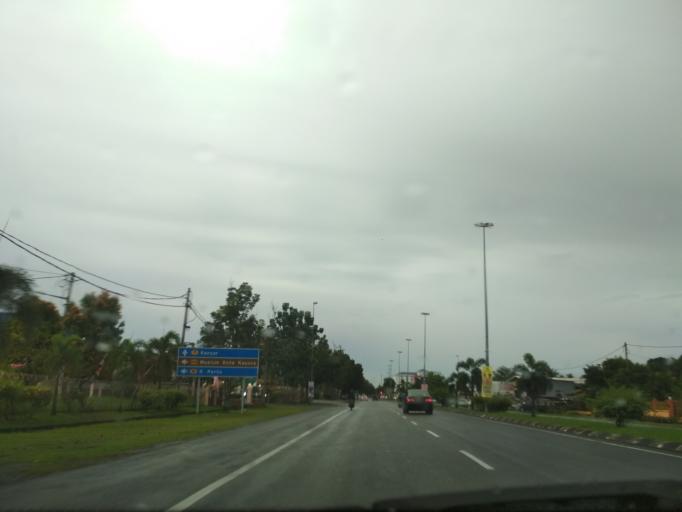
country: MY
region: Perlis
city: Kangar
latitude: 6.4245
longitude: 100.1844
